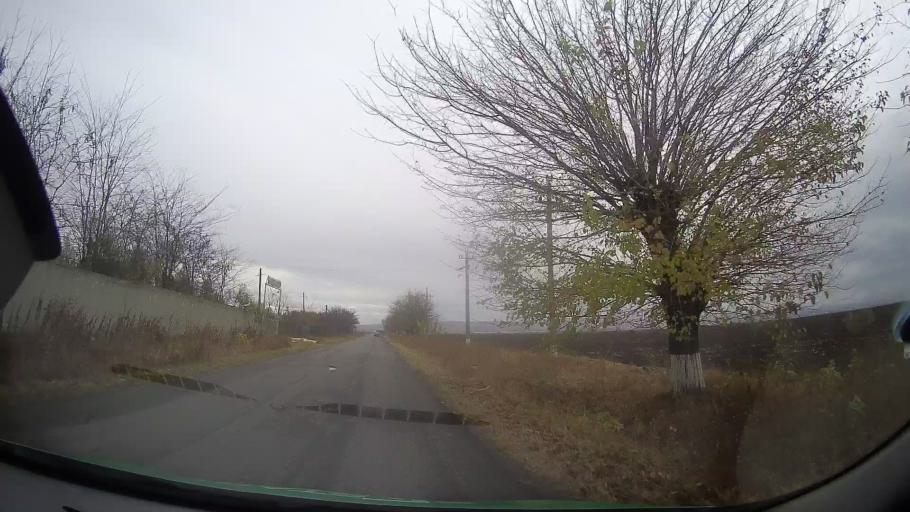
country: RO
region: Prahova
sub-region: Comuna Colceag
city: Inotesti
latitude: 44.9730
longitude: 26.3425
